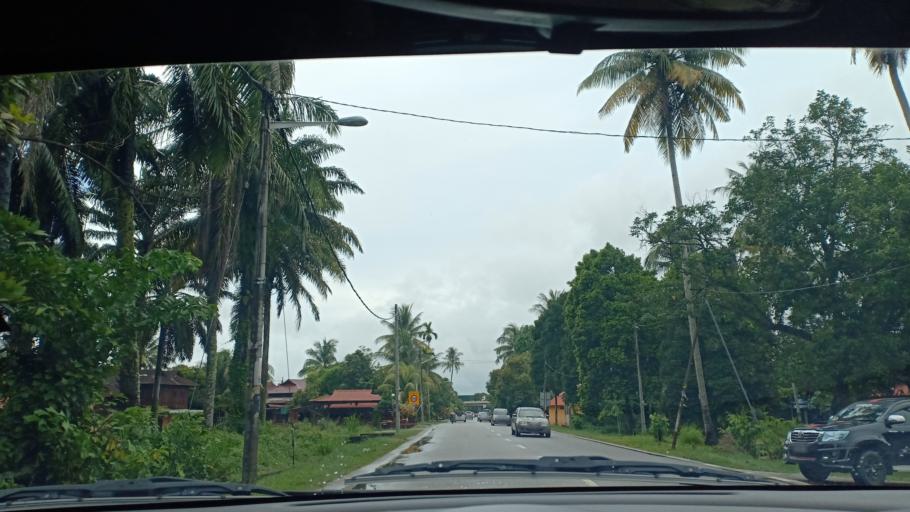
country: MY
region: Penang
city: Kepala Batas
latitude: 5.4973
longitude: 100.4393
